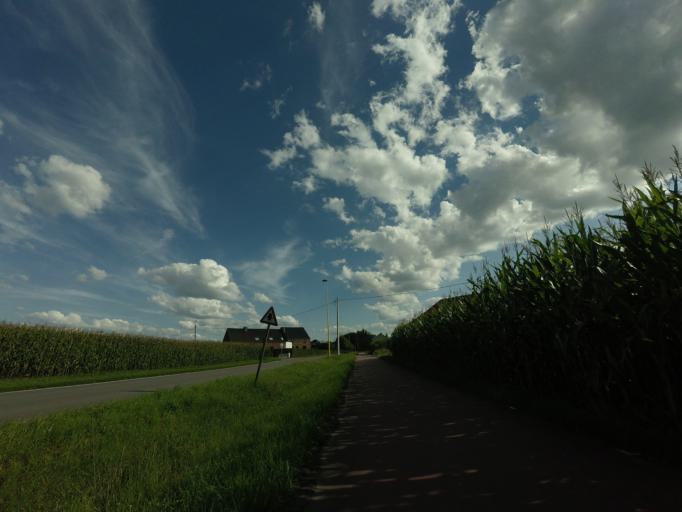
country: BE
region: Flanders
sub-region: Provincie Vlaams-Brabant
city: Meise
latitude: 50.9697
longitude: 4.3489
